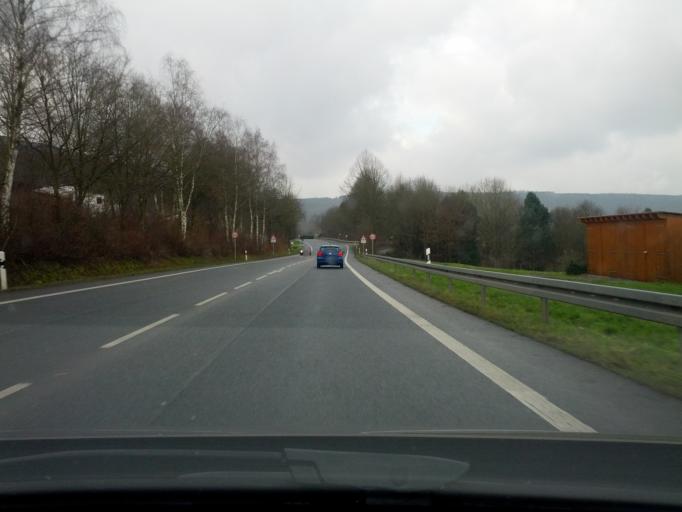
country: DE
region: Lower Saxony
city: Bodenfelde
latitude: 51.5929
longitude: 9.5612
